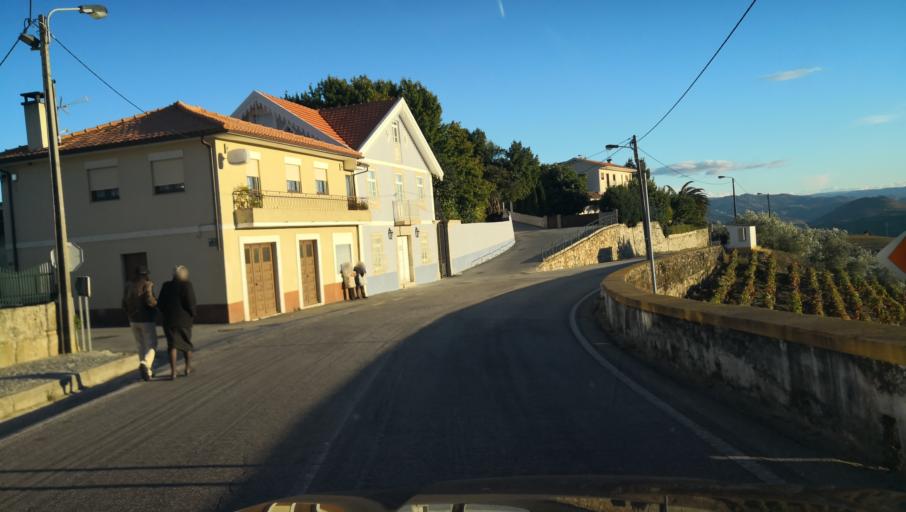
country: PT
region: Vila Real
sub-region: Santa Marta de Penaguiao
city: Santa Marta de Penaguiao
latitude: 41.2515
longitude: -7.7713
